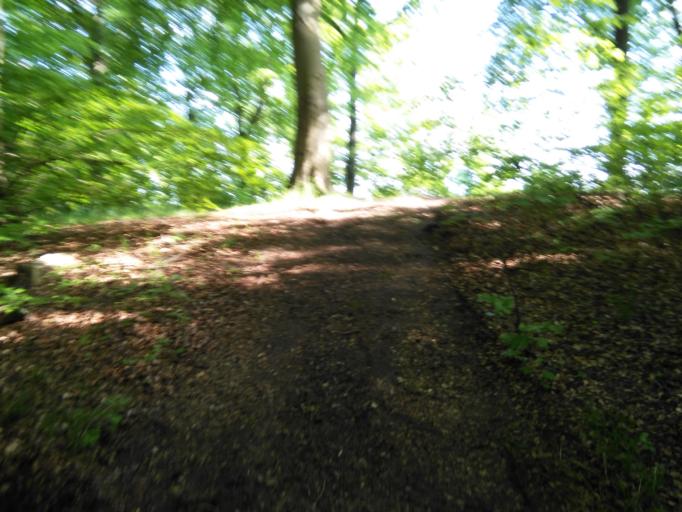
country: DK
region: Central Jutland
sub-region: Arhus Kommune
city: Arhus
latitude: 56.1216
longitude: 10.2228
